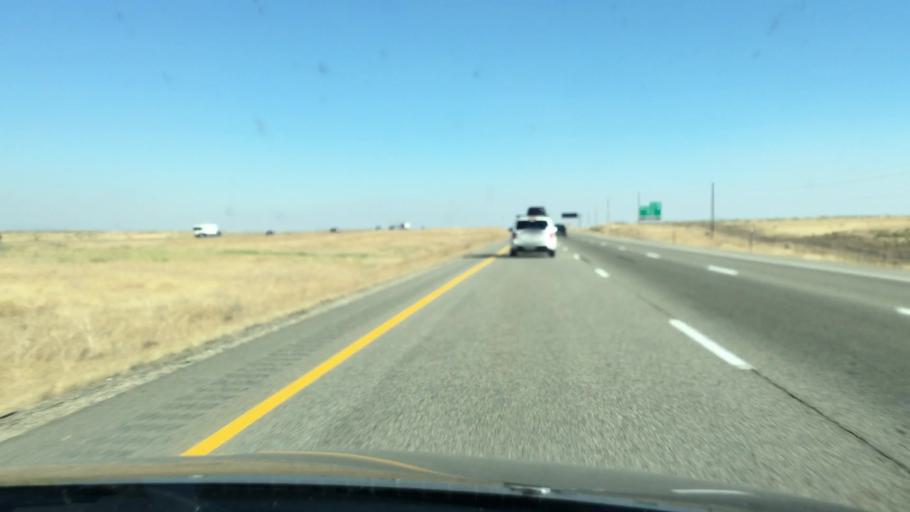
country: US
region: Idaho
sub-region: Ada County
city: Boise
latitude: 43.4744
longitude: -116.1034
